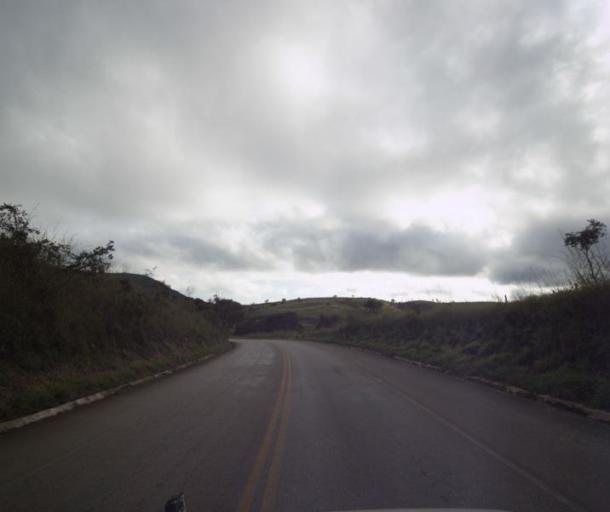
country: BR
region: Goias
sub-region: Pirenopolis
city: Pirenopolis
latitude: -15.7305
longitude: -48.7081
